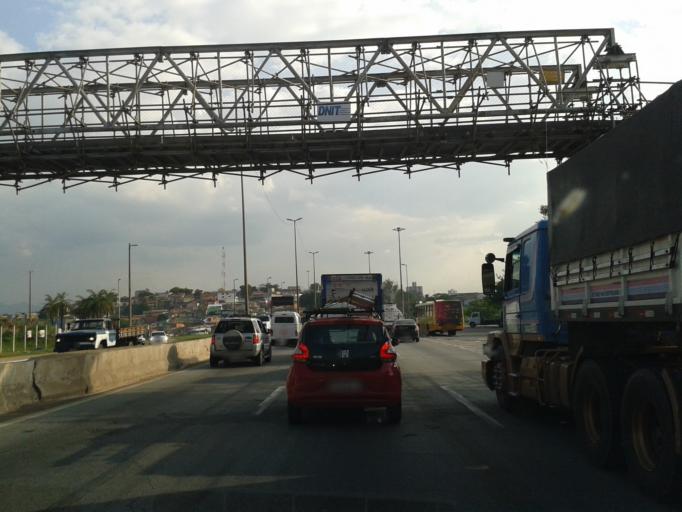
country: BR
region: Minas Gerais
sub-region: Belo Horizonte
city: Belo Horizonte
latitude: -19.8766
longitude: -43.9508
